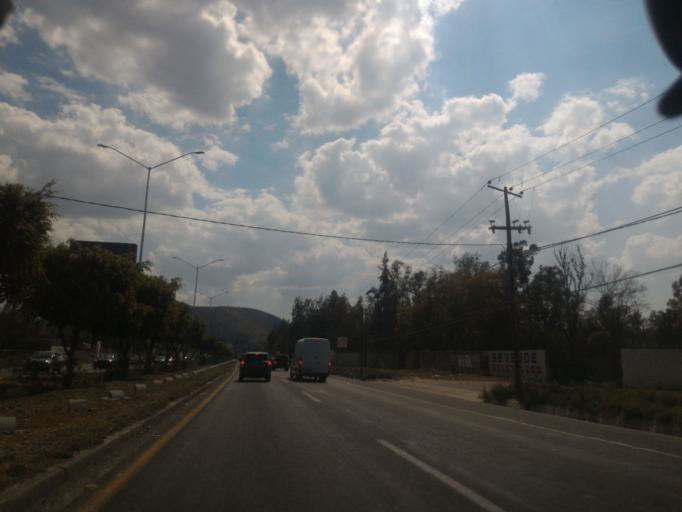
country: MX
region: Jalisco
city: Nicolas R Casillas
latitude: 20.5411
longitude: -103.4735
